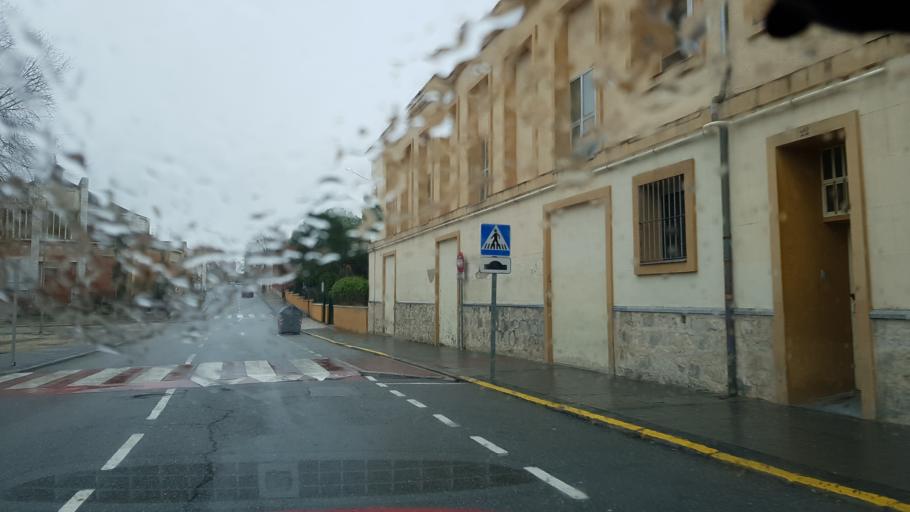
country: ES
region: Castille and Leon
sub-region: Provincia de Segovia
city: Segovia
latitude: 40.9410
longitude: -4.1050
